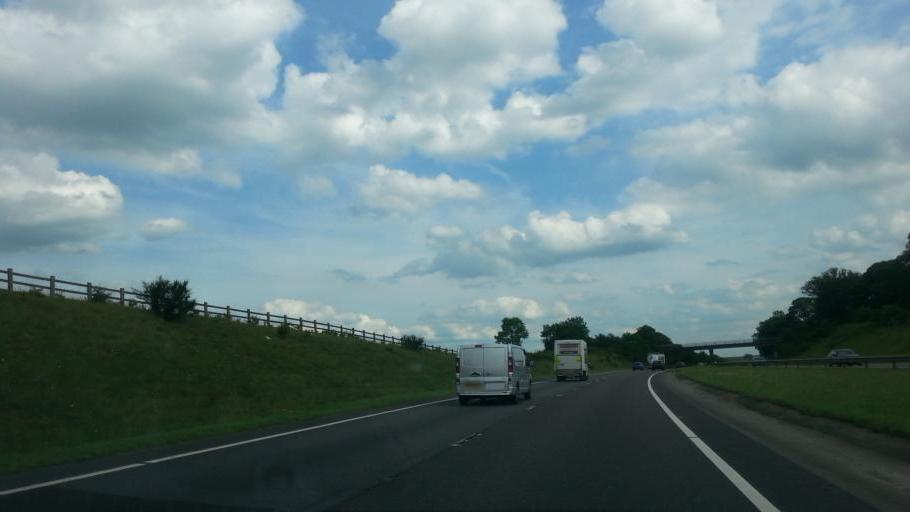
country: GB
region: England
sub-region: Nottinghamshire
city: Bircotes
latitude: 53.3857
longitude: -1.0592
